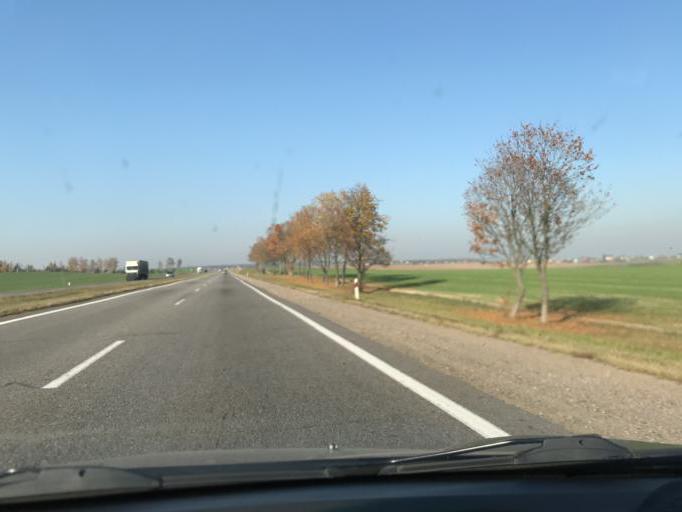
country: BY
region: Minsk
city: Luhavaya Slabada
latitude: 53.7402
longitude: 27.8435
